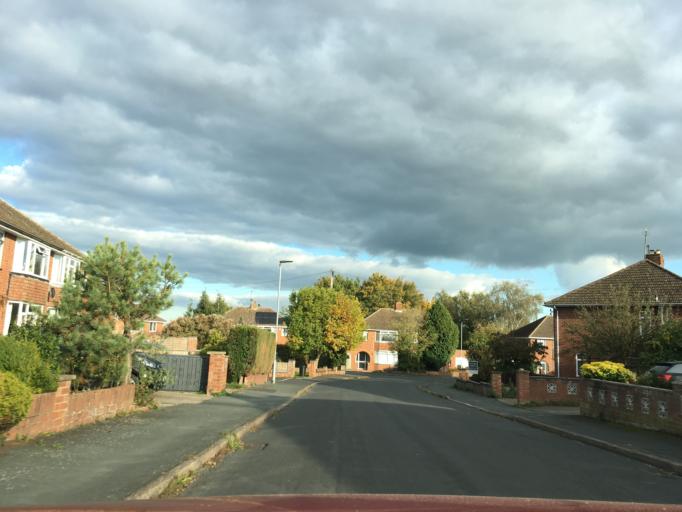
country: GB
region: England
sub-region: Herefordshire
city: Hereford
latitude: 52.0595
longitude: -2.6871
